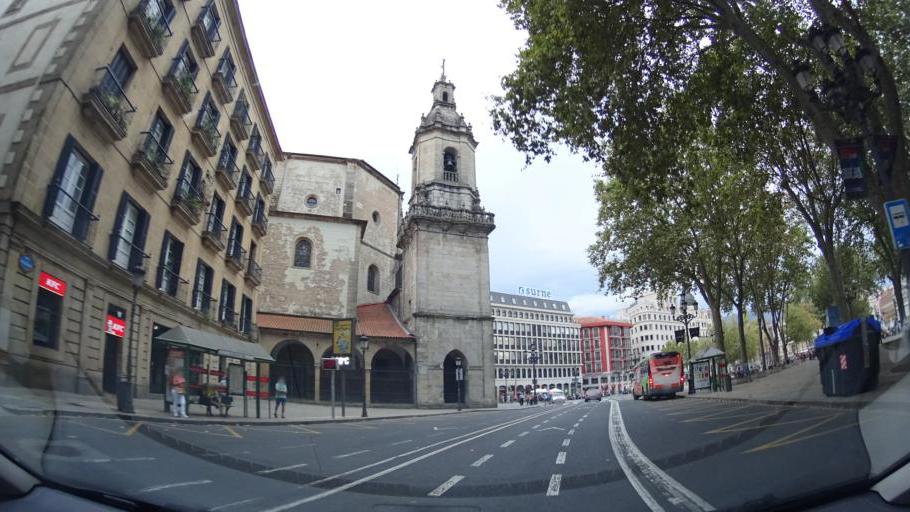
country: ES
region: Basque Country
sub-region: Bizkaia
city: Bilbao
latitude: 43.2606
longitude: -2.9228
